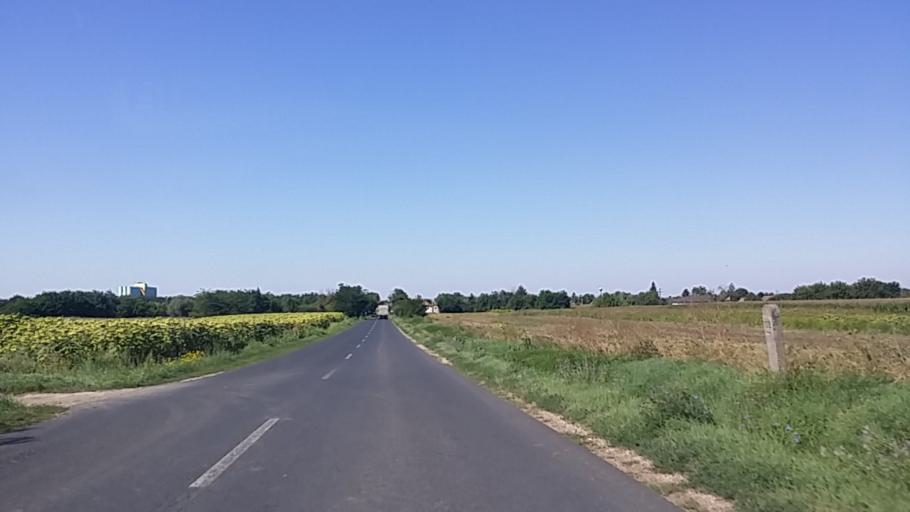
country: HU
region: Fejer
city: Sarbogard
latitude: 46.8638
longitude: 18.6442
